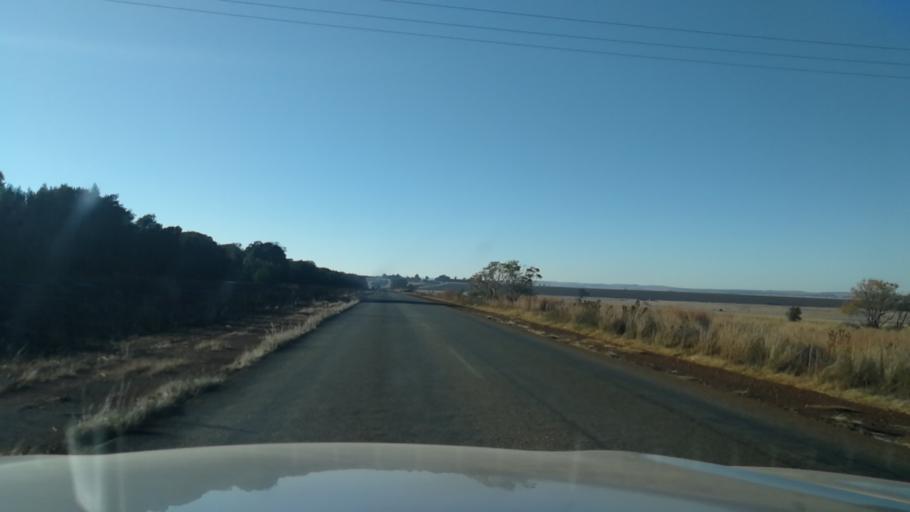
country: ZA
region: North-West
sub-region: Bojanala Platinum District Municipality
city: Koster
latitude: -25.9402
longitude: 27.1577
